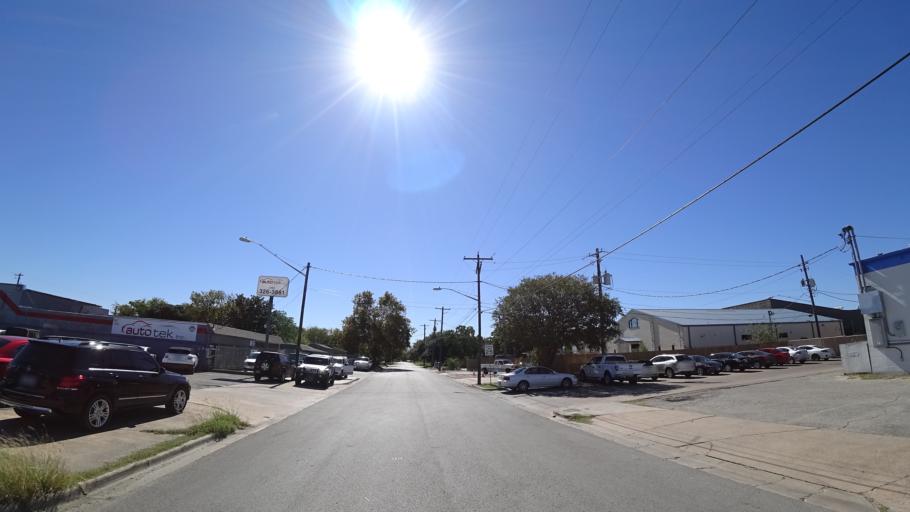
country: US
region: Texas
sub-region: Travis County
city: Rollingwood
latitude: 30.2270
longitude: -97.7817
